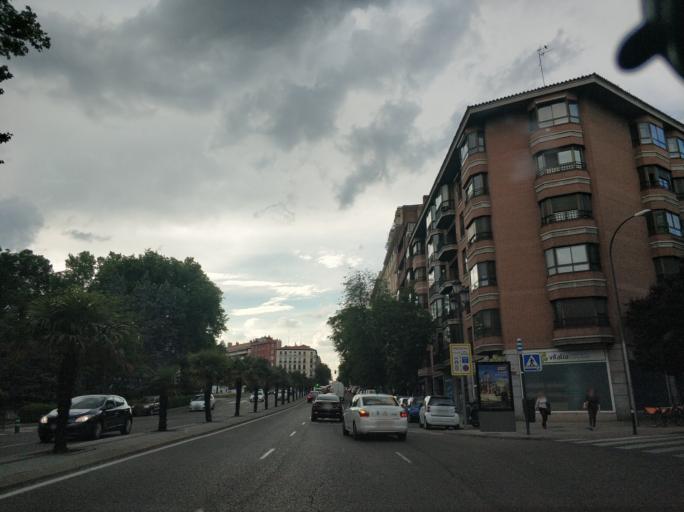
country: ES
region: Madrid
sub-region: Provincia de Madrid
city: City Center
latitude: 40.4236
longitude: -3.7148
